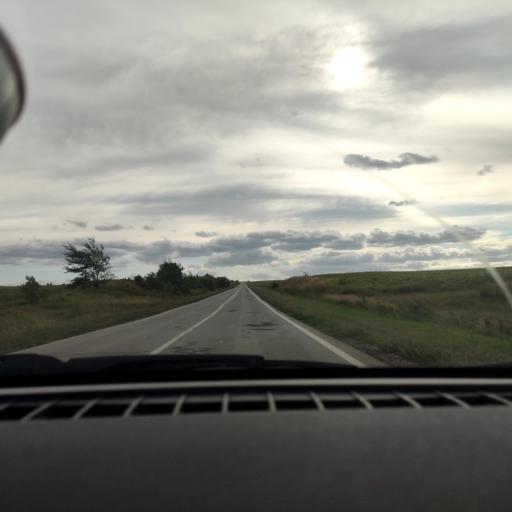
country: RU
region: Samara
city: Krasnyy Yar
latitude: 53.4364
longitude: 50.5720
